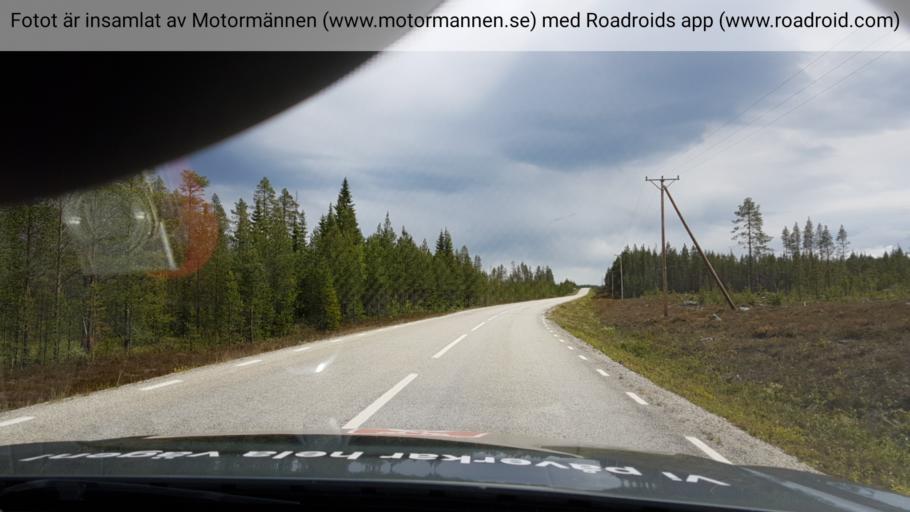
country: SE
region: Jaemtland
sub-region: Are Kommun
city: Jarpen
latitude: 62.8083
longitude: 13.6561
